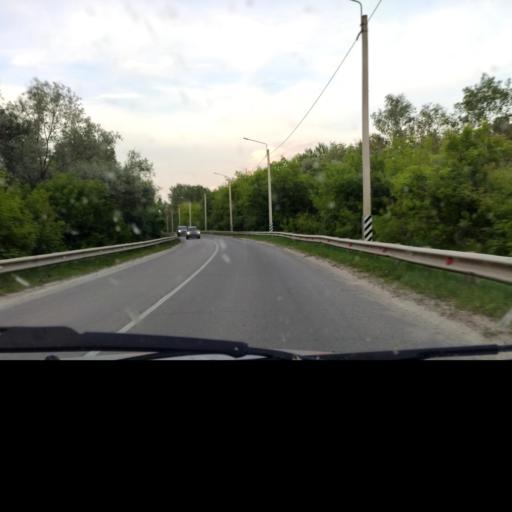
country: RU
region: Voronezj
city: Ramon'
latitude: 51.9489
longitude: 39.3763
